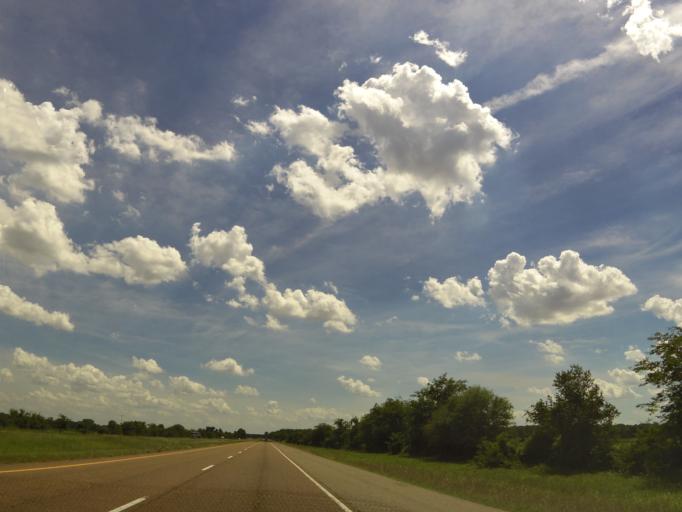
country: US
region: Tennessee
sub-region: Dyer County
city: Dyersburg
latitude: 36.0461
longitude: -89.3359
